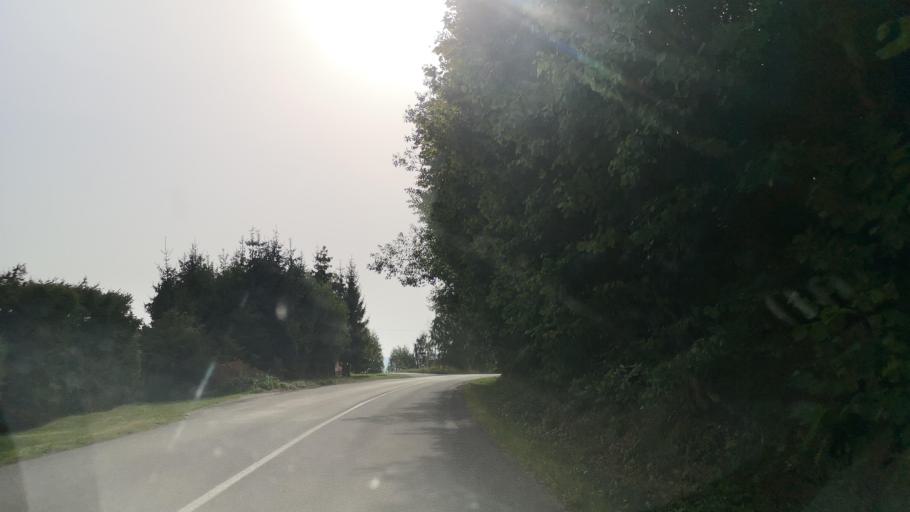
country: SK
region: Banskobystricky
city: Poltar
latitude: 48.5931
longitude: 19.7328
